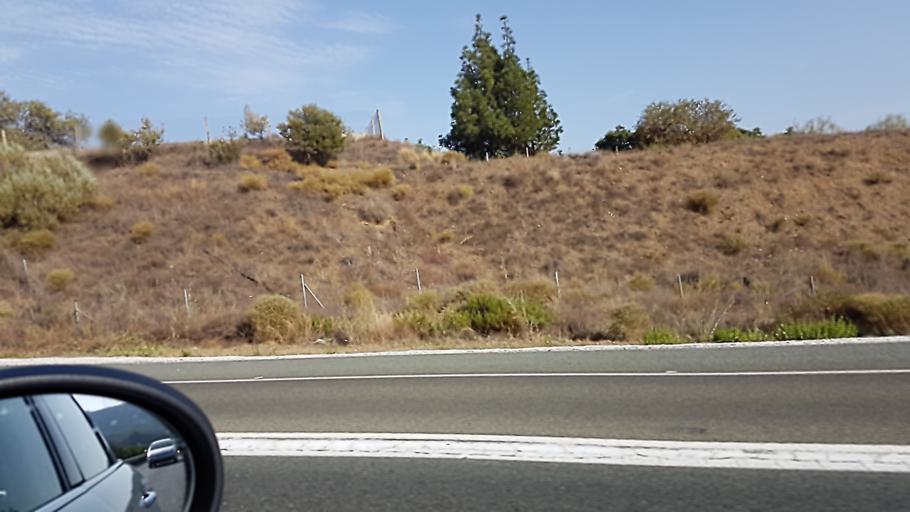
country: ES
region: Andalusia
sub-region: Provincia de Malaga
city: Iznate
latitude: 36.7439
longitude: -4.1826
